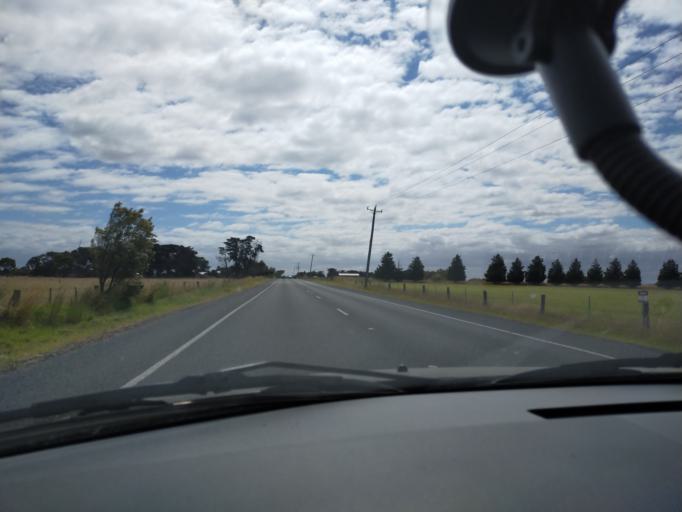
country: AU
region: Victoria
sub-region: Greater Geelong
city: Breakwater
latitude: -38.2547
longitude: 144.3853
